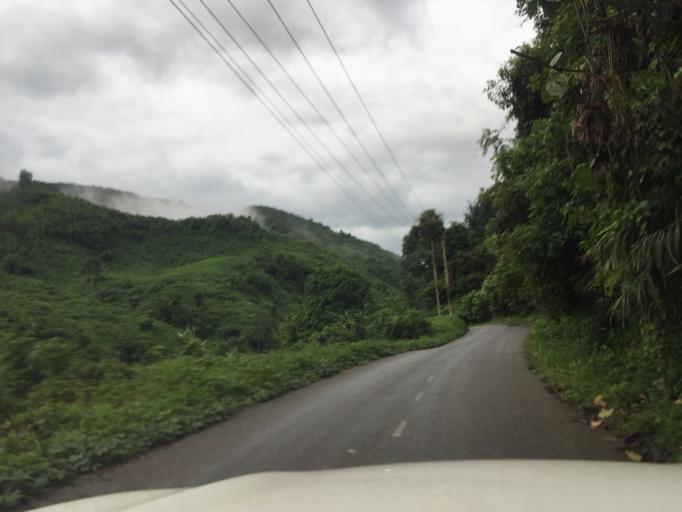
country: LA
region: Oudomxai
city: Muang La
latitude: 21.0308
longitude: 102.2368
